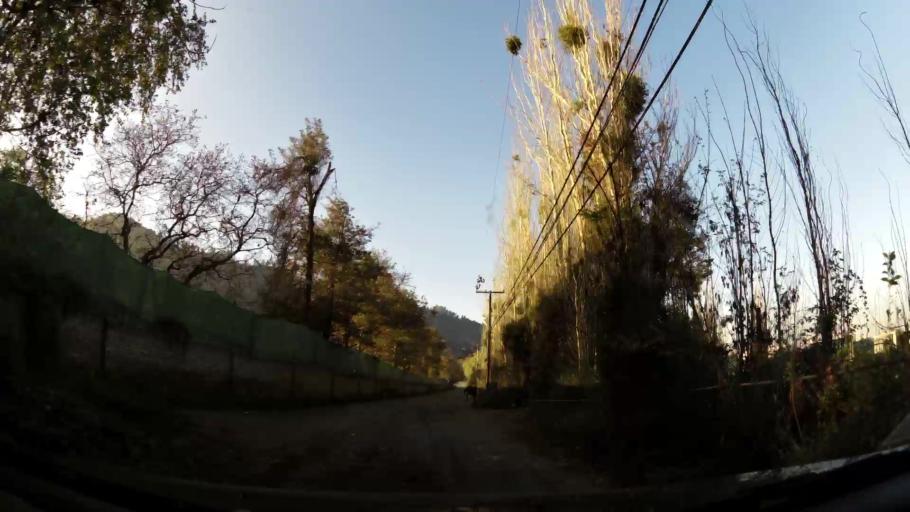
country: CL
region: Santiago Metropolitan
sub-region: Provincia de Santiago
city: Santiago
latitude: -33.3871
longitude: -70.6113
